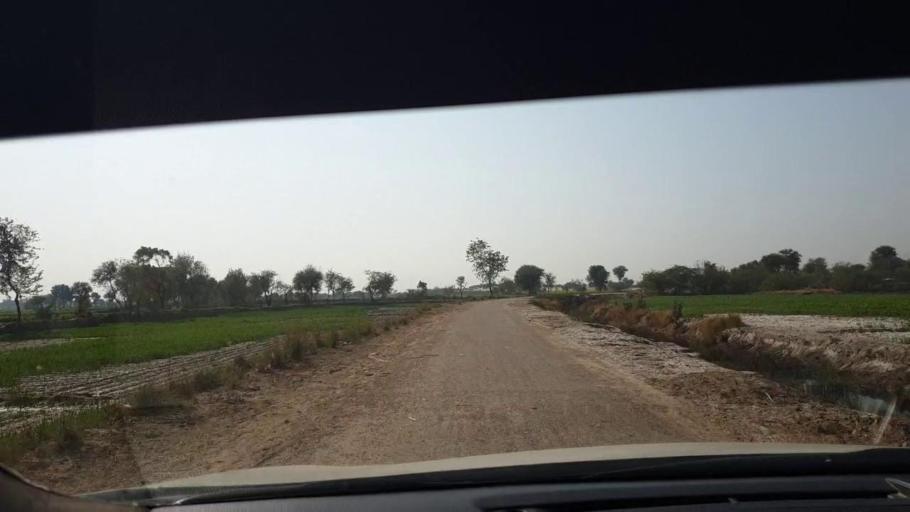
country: PK
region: Sindh
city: Tando Adam
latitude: 25.7345
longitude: 68.6973
